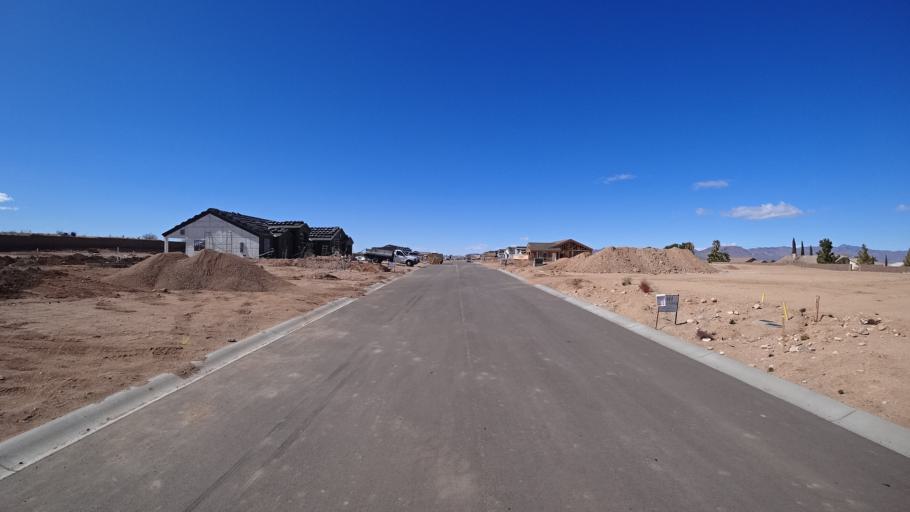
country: US
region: Arizona
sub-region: Mohave County
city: Kingman
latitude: 35.1966
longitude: -113.9623
